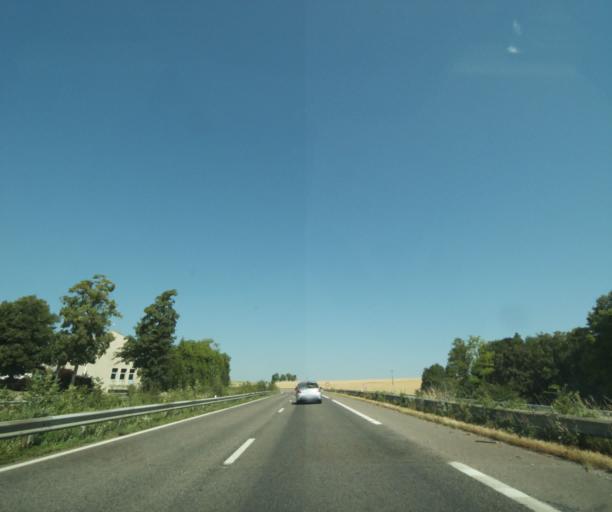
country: FR
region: Lorraine
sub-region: Departement de la Meuse
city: Vacon
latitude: 48.7029
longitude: 5.5315
